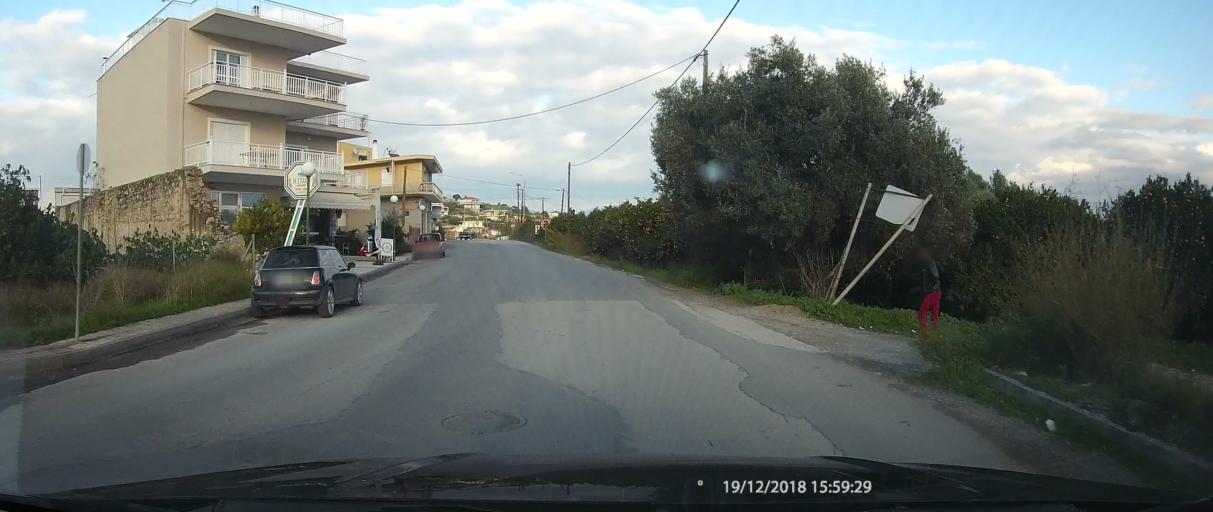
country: GR
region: Peloponnese
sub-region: Nomos Lakonias
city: Skala
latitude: 36.8525
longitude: 22.6732
